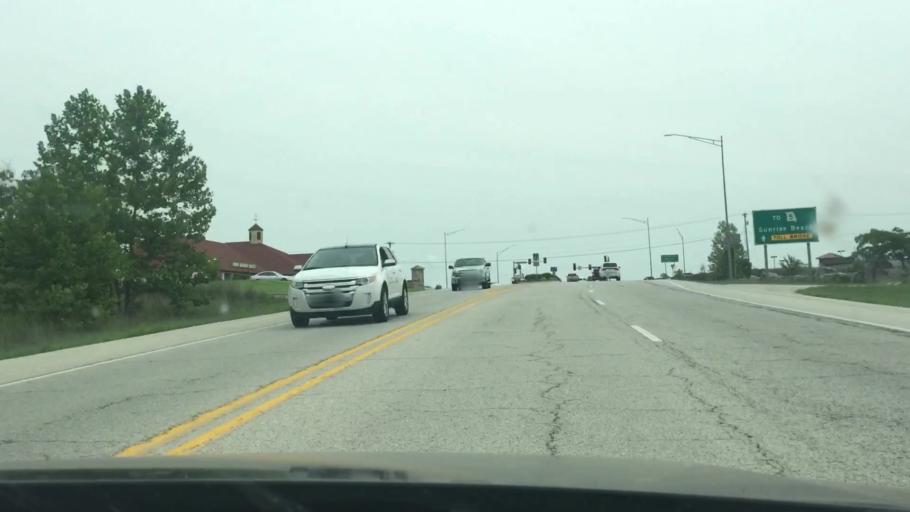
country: US
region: Missouri
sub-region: Miller County
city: Lake Ozark
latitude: 38.1913
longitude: -92.6470
